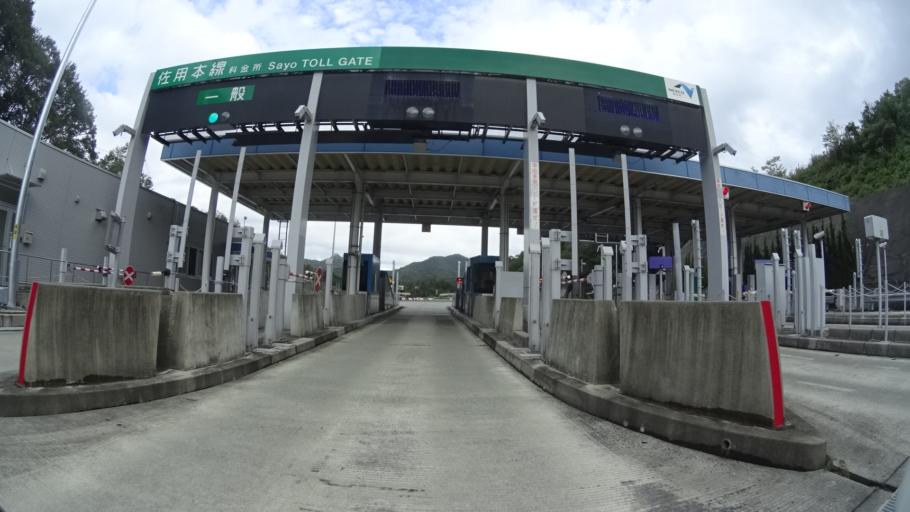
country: JP
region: Hyogo
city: Yamazakicho-nakabirose
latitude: 35.0299
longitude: 134.3884
